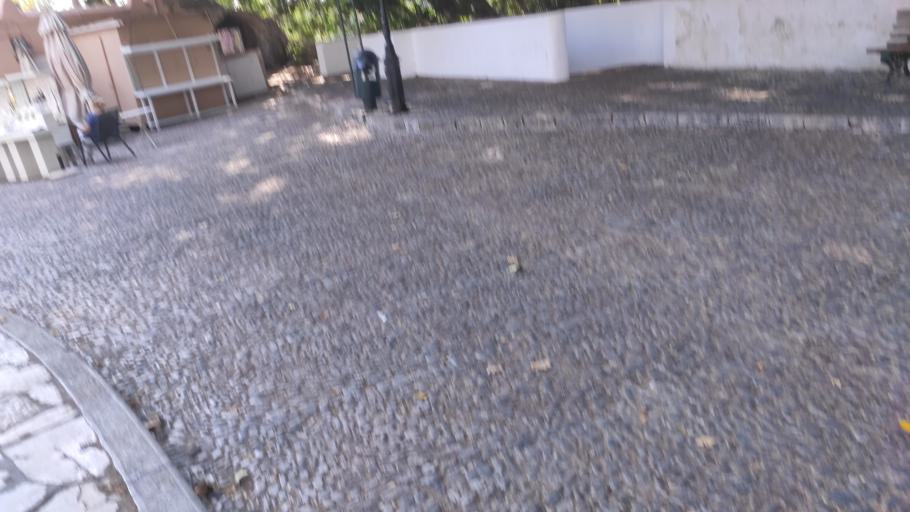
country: GR
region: South Aegean
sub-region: Nomos Dodekanisou
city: Kos
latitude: 36.8948
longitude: 27.2910
